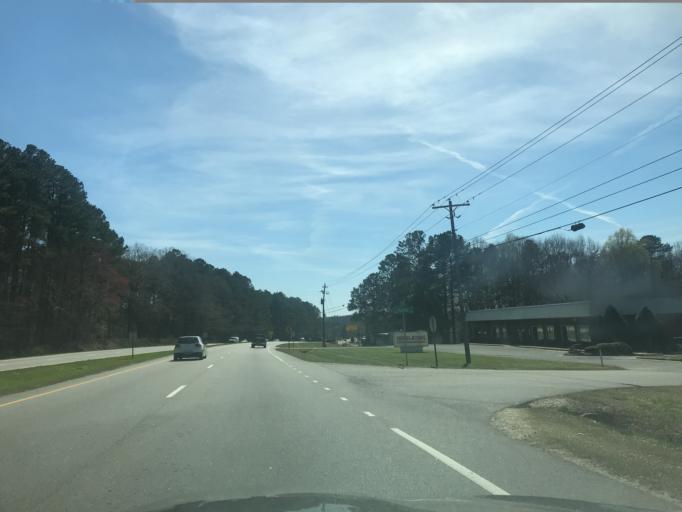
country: US
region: North Carolina
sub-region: Wake County
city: Garner
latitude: 35.6975
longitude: -78.6724
